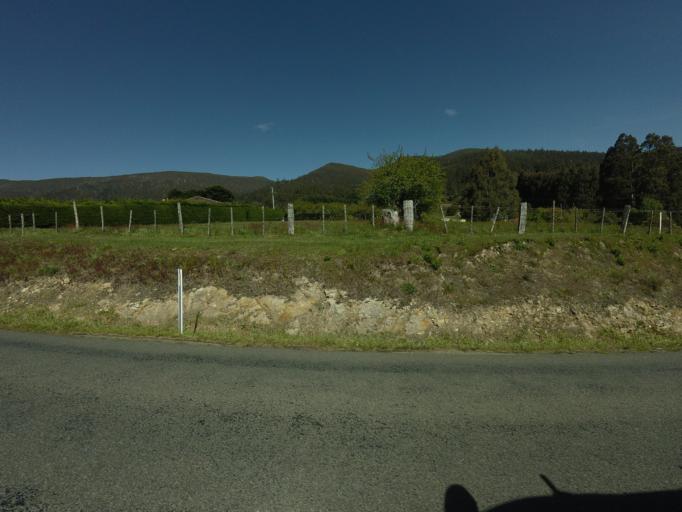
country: AU
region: Tasmania
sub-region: Derwent Valley
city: New Norfolk
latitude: -42.7515
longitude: 146.6365
